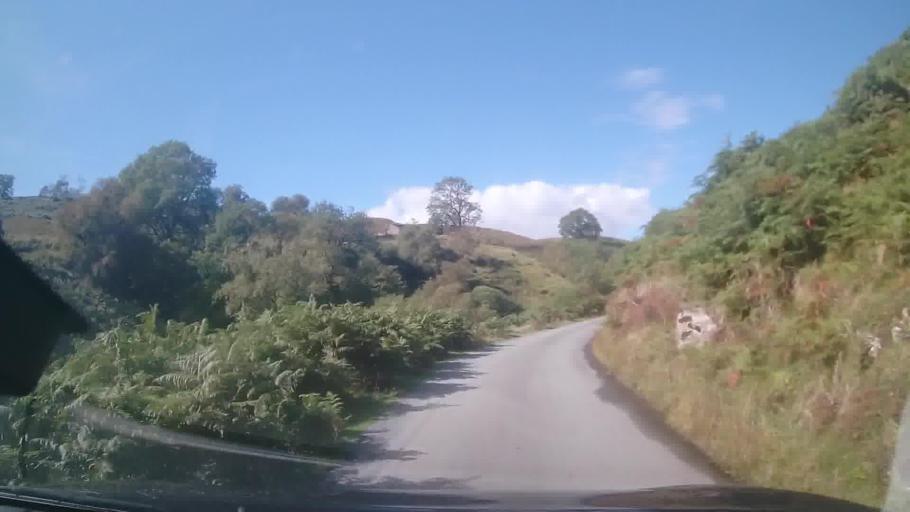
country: GB
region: Wales
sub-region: Gwynedd
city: Bala
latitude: 52.7940
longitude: -3.5640
